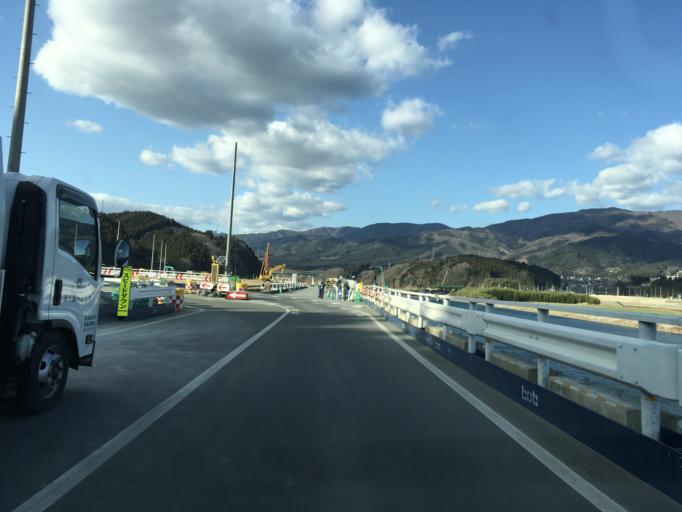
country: JP
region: Iwate
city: Ofunato
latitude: 39.0130
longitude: 141.6163
